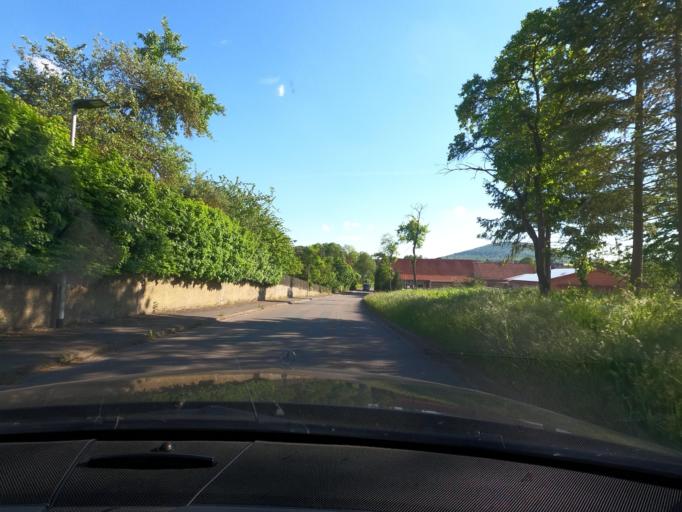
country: DE
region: Hesse
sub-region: Regierungsbezirk Kassel
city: Martinhagen
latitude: 51.3340
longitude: 9.2460
